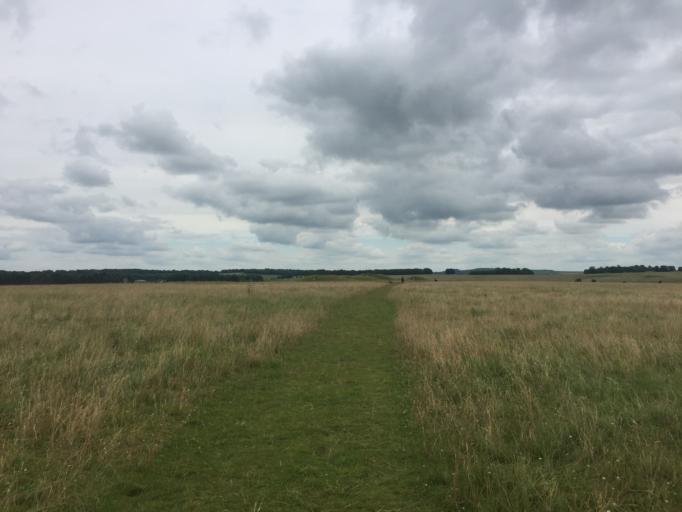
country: GB
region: England
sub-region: Wiltshire
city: Durnford
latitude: 51.1836
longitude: -1.8357
